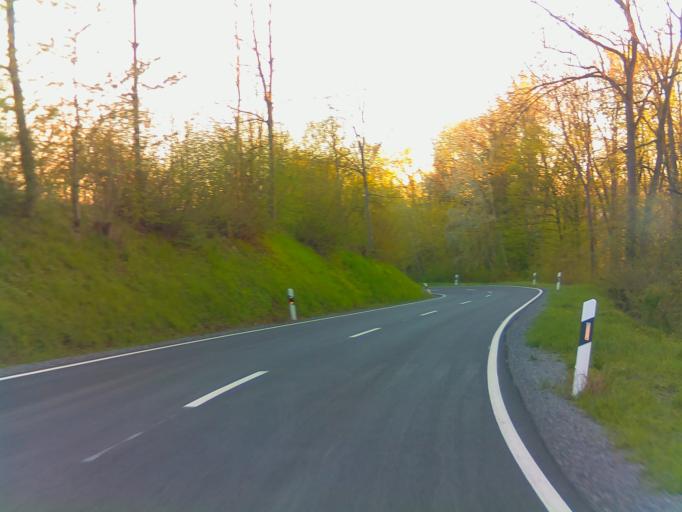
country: DE
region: Baden-Wuerttemberg
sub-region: Regierungsbezirk Stuttgart
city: Pfedelbach
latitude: 49.1647
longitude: 9.4977
